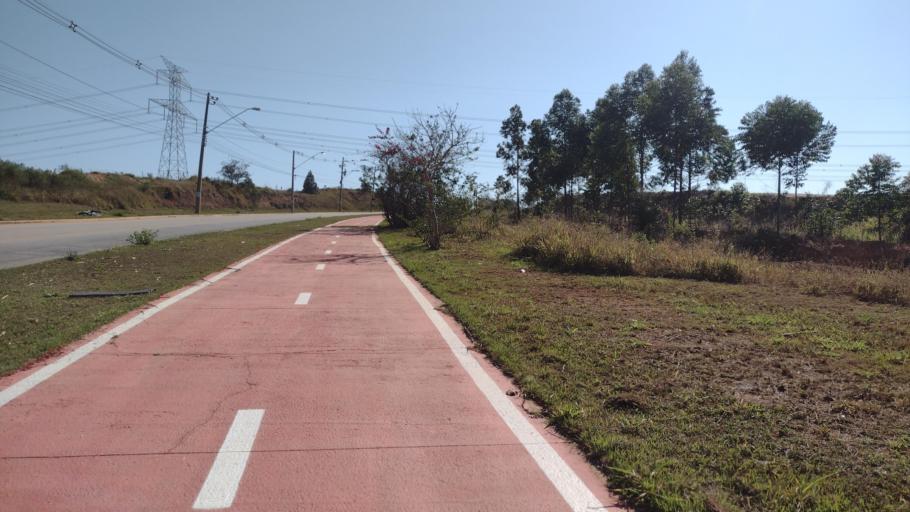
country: BR
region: Sao Paulo
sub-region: Sorocaba
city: Sorocaba
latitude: -23.4014
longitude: -47.4785
